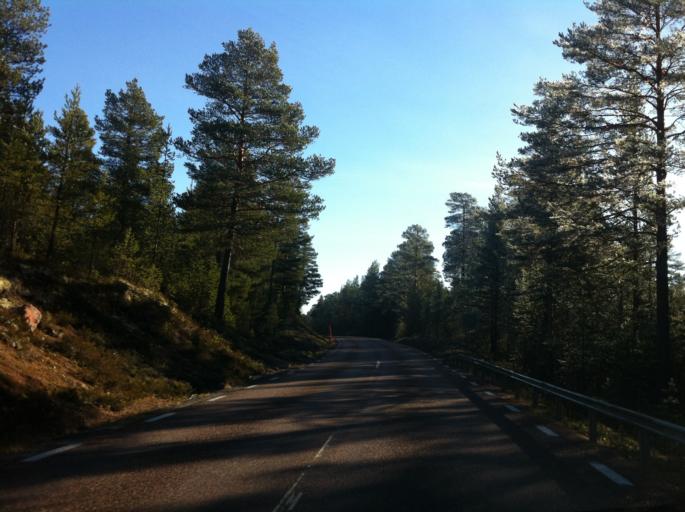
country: NO
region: Hedmark
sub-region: Trysil
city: Innbygda
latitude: 61.8469
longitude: 12.7710
